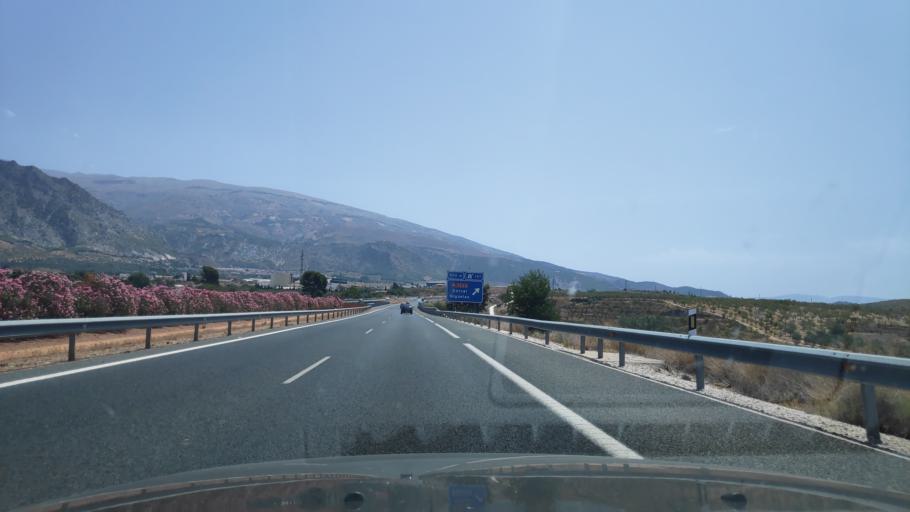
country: ES
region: Andalusia
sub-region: Provincia de Granada
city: Durcal
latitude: 36.9805
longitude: -3.5725
